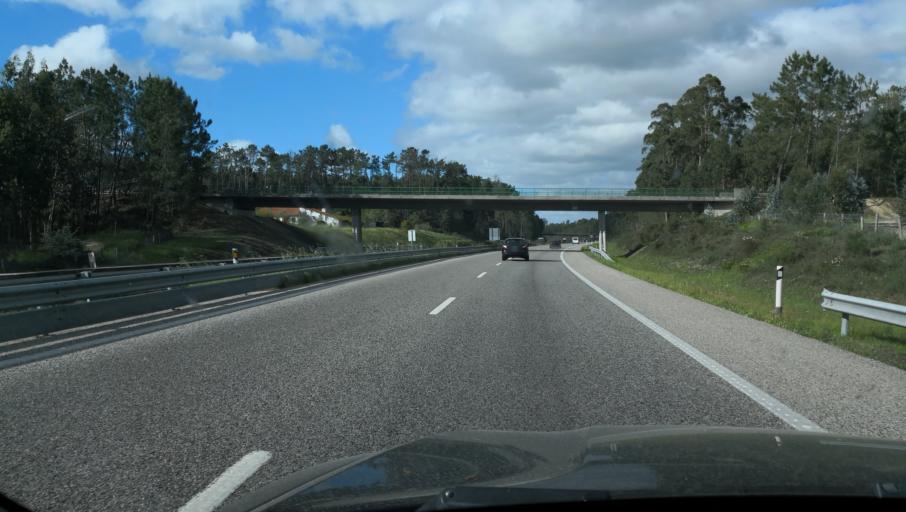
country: PT
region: Leiria
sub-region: Pombal
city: Pombal
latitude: 39.9186
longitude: -8.6839
